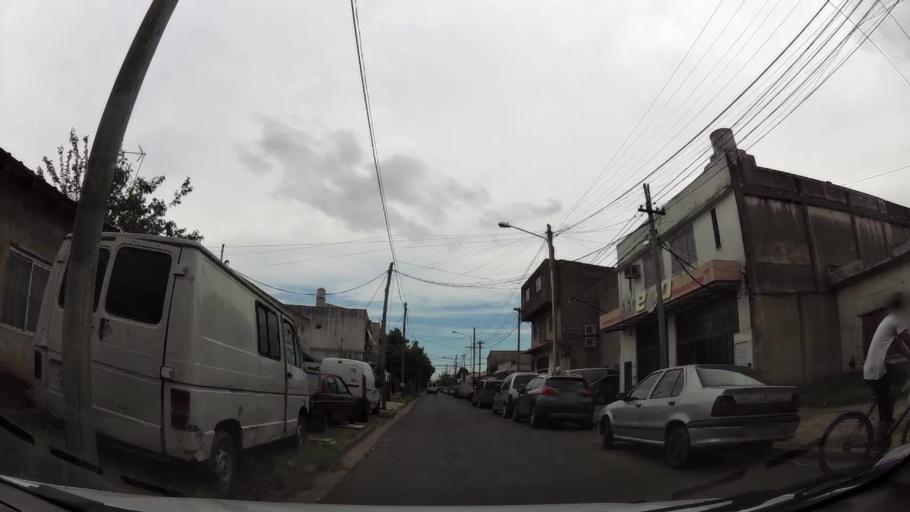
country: AR
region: Buenos Aires
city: San Justo
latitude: -34.6647
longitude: -58.5308
